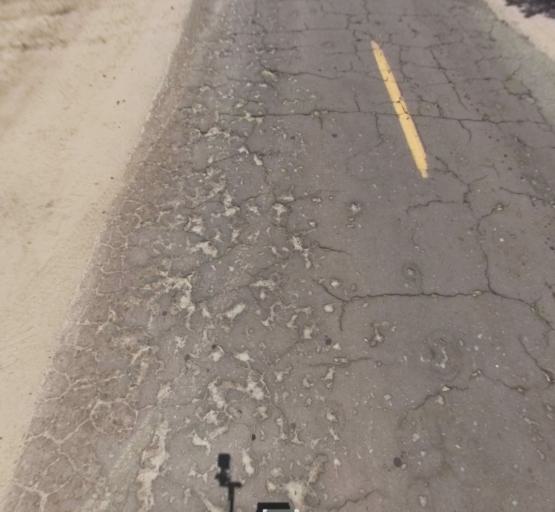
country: US
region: California
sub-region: Fresno County
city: Biola
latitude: 36.8338
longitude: -120.1510
